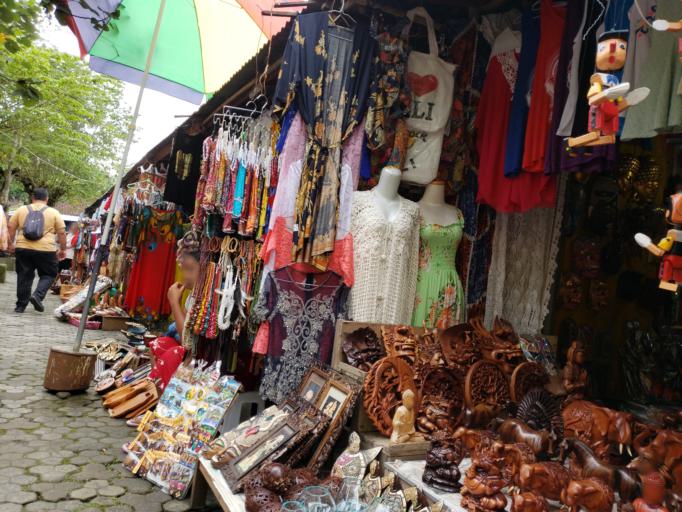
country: ID
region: Bali
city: Banjar Manukayaanyar
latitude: -8.4160
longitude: 115.3158
